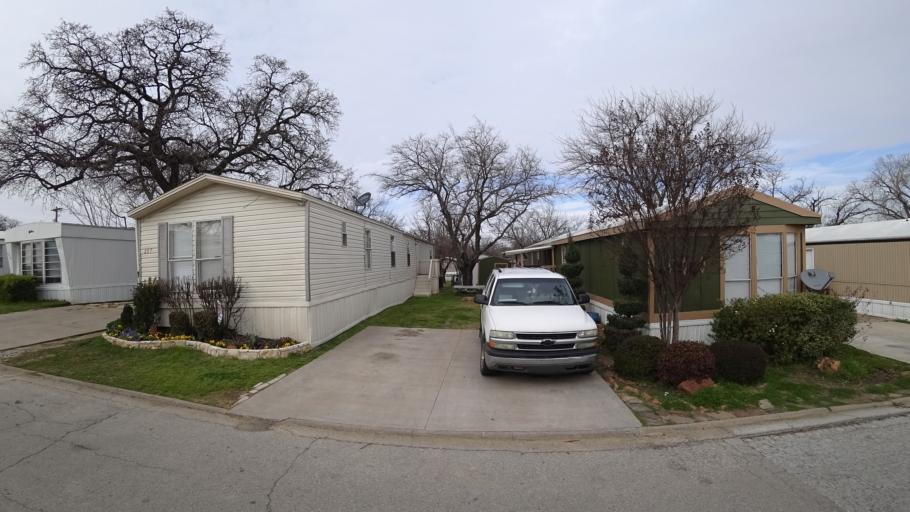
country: US
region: Texas
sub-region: Denton County
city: Lewisville
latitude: 33.0323
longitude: -96.9868
